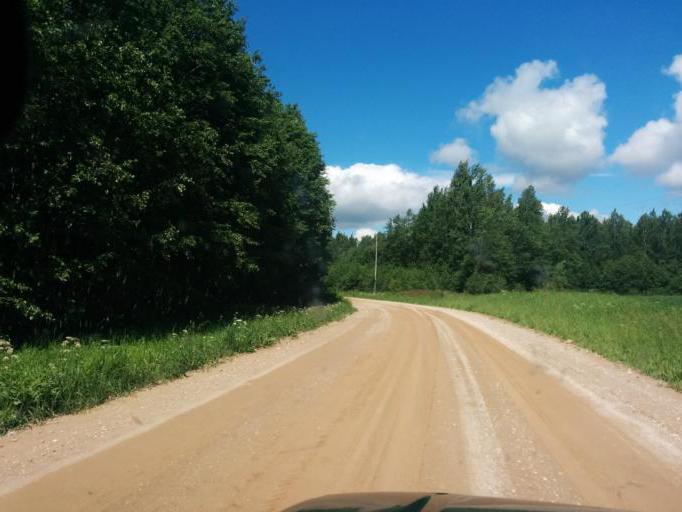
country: LV
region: Vilaka
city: Vilaka
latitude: 57.3738
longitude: 27.4684
